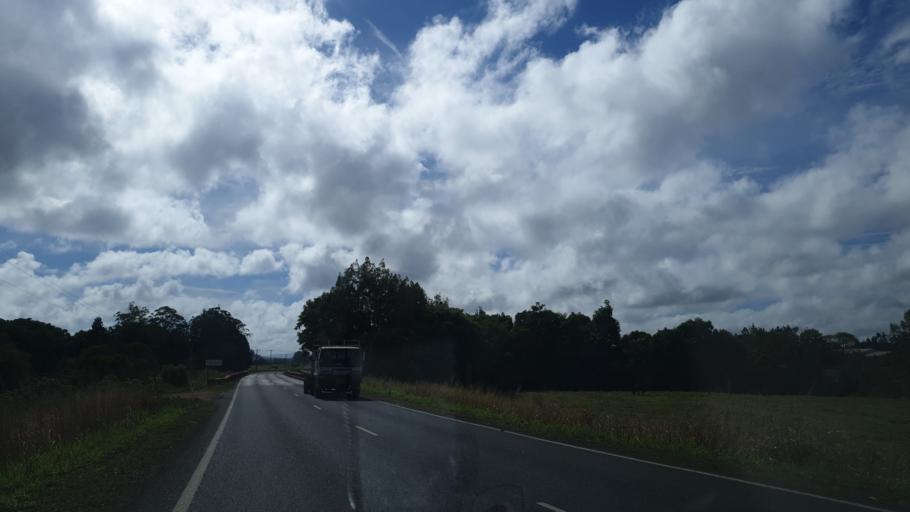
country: AU
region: Queensland
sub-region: Tablelands
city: Atherton
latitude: -17.2943
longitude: 145.5325
